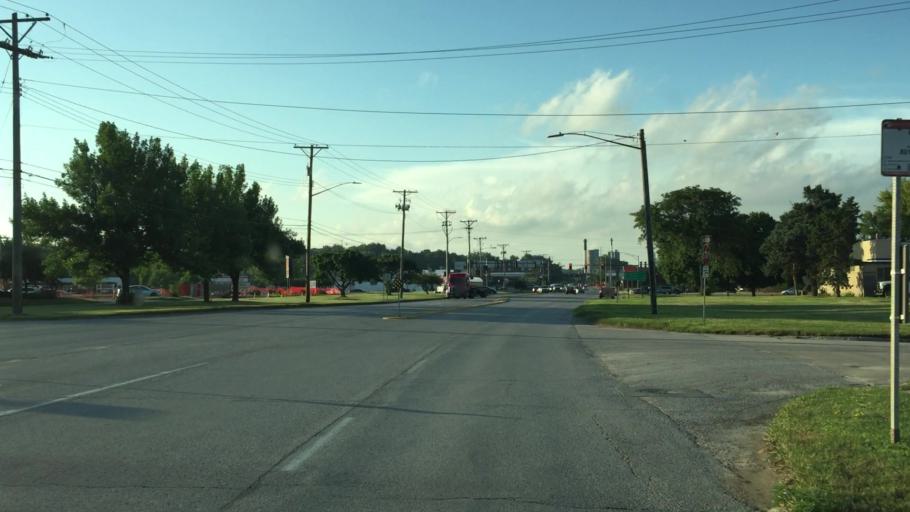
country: US
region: Iowa
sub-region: Johnson County
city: Iowa City
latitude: 41.6458
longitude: -91.5400
